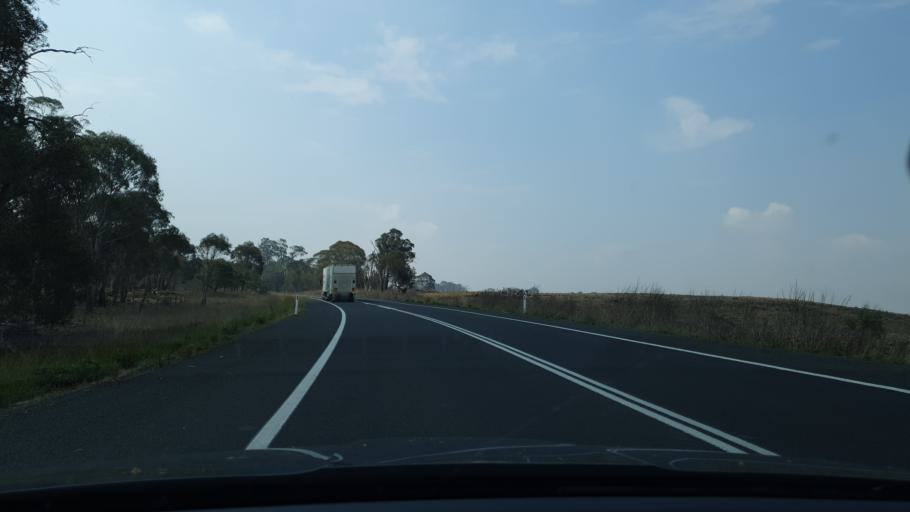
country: AU
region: New South Wales
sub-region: Guyra
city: Guyra
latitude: -30.0834
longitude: 151.7207
